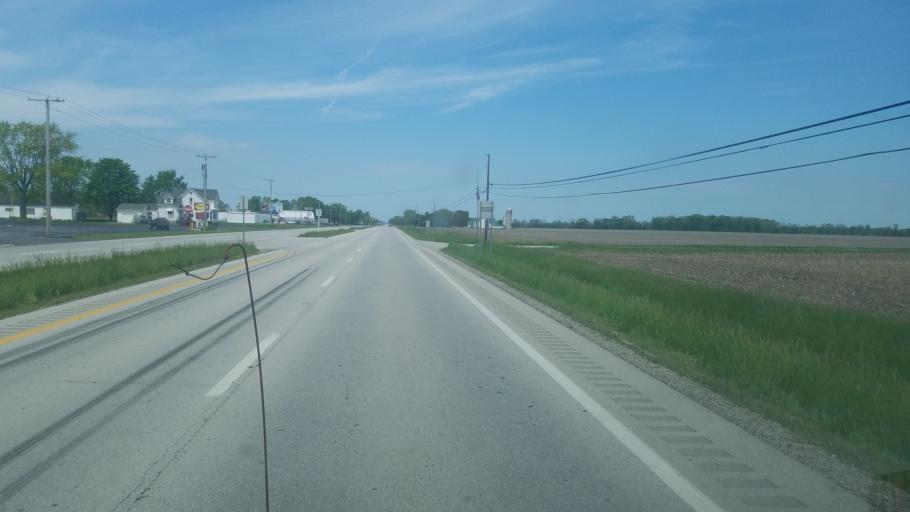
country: US
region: Ohio
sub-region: Sandusky County
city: Stony Prairie
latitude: 41.3766
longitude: -83.1836
